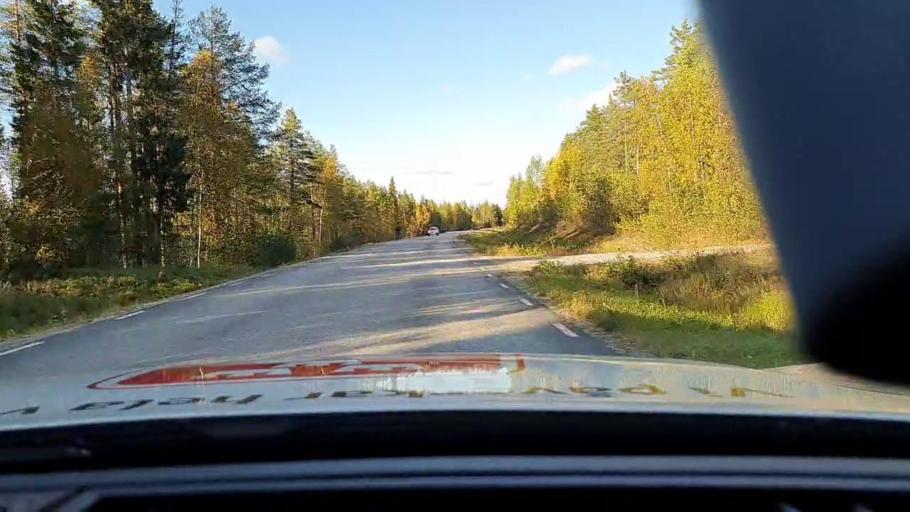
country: SE
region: Norrbotten
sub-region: Pitea Kommun
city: Norrfjarden
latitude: 65.4992
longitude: 21.4757
